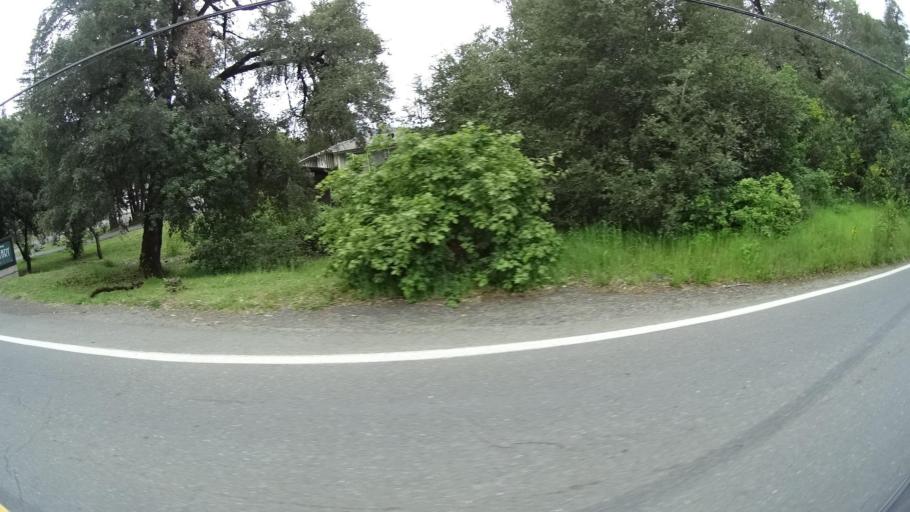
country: US
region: California
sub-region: Humboldt County
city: Redway
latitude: 40.1067
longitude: -123.7913
